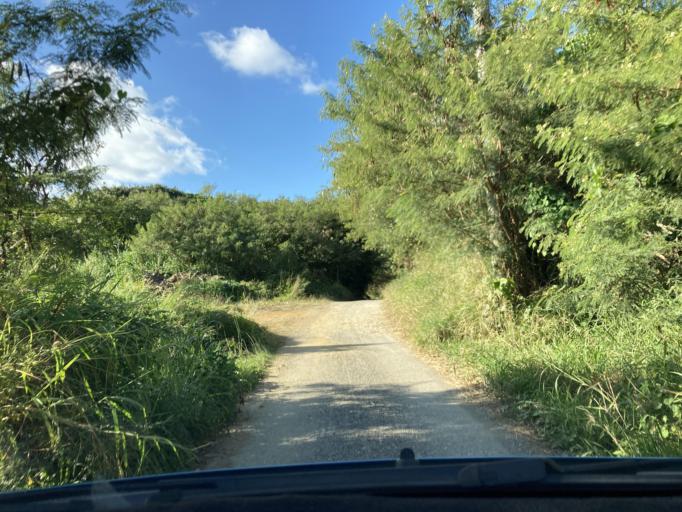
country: JP
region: Okinawa
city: Katsuren-haebaru
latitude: 26.3197
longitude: 127.9242
